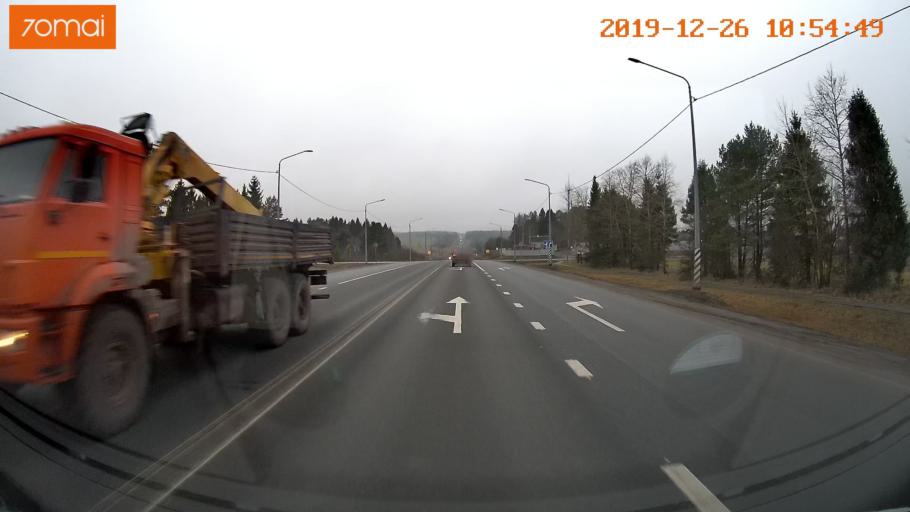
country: RU
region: Vologda
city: Molochnoye
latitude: 59.1893
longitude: 39.5921
